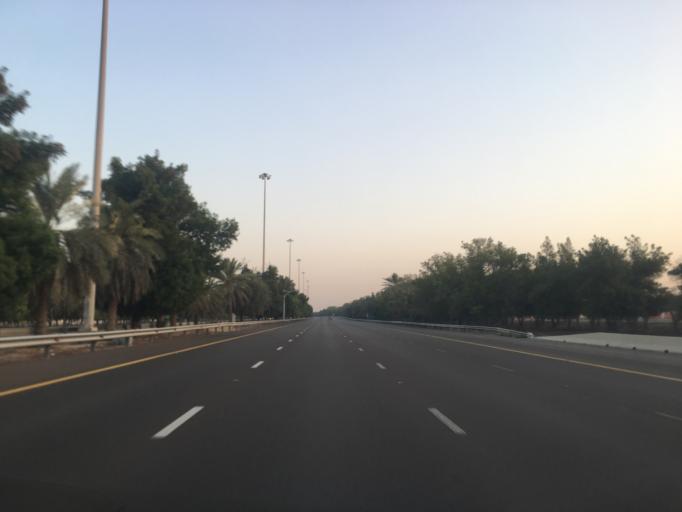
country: AE
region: Abu Dhabi
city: Abu Dhabi
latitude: 24.3560
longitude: 54.5674
